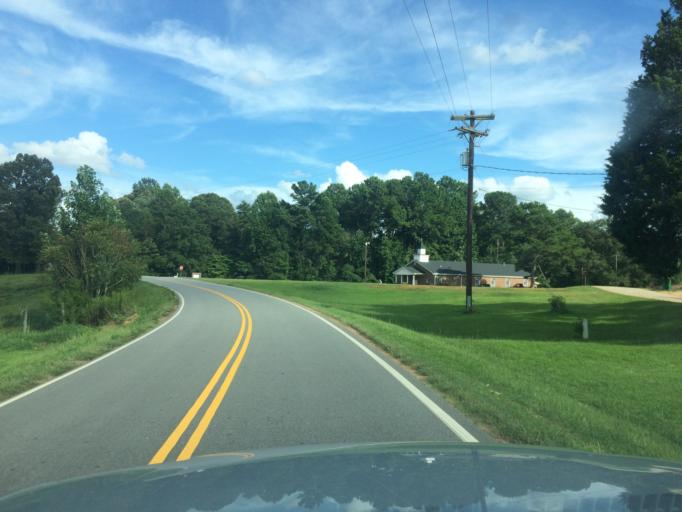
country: US
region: South Carolina
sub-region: Greenville County
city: Fountain Inn
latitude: 34.7390
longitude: -82.1258
